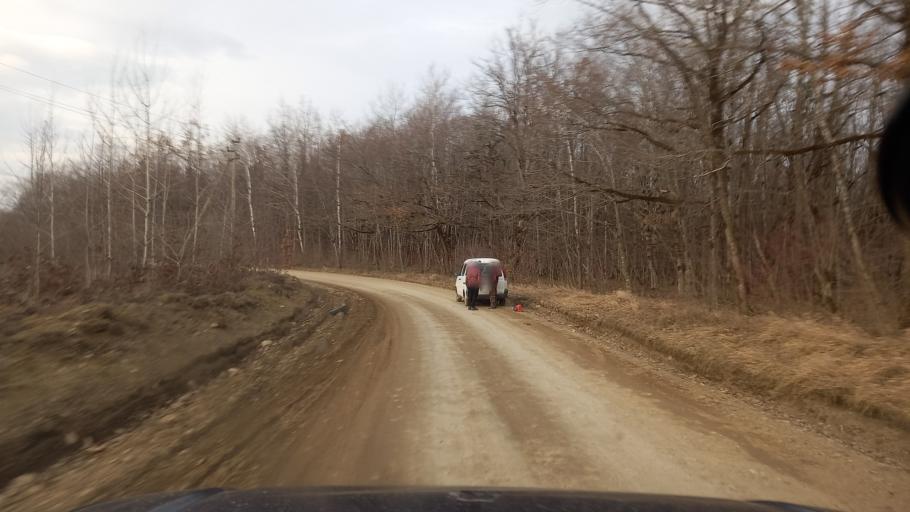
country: RU
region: Adygeya
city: Kamennomostskiy
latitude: 44.1610
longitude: 40.2451
